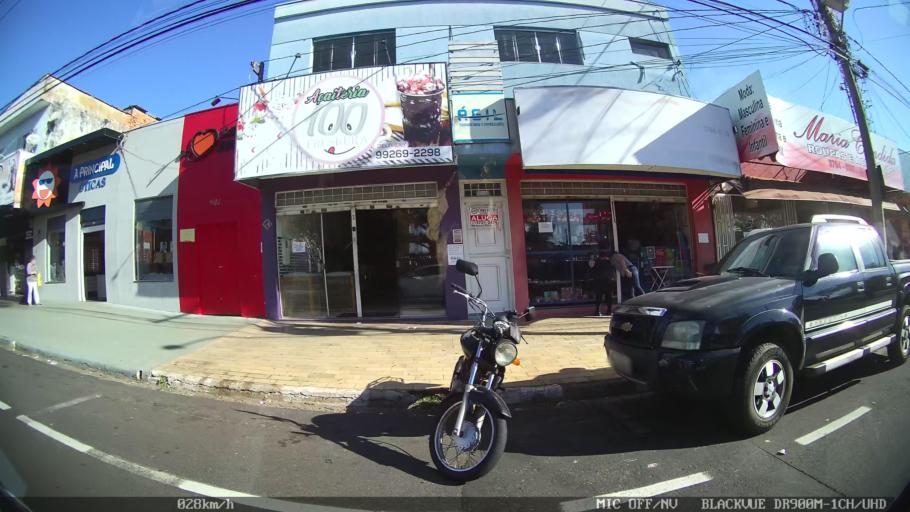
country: BR
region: Sao Paulo
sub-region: Franca
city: Franca
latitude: -20.4988
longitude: -47.4175
